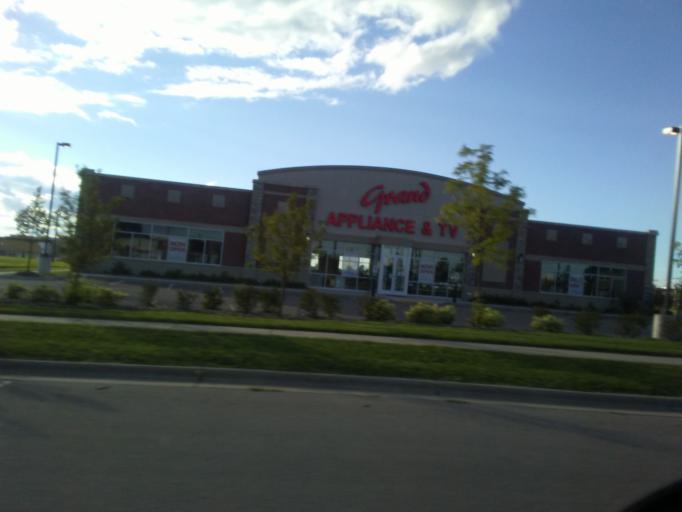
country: US
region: Wisconsin
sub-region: Dane County
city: Sun Prairie
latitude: 43.1674
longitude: -89.2668
